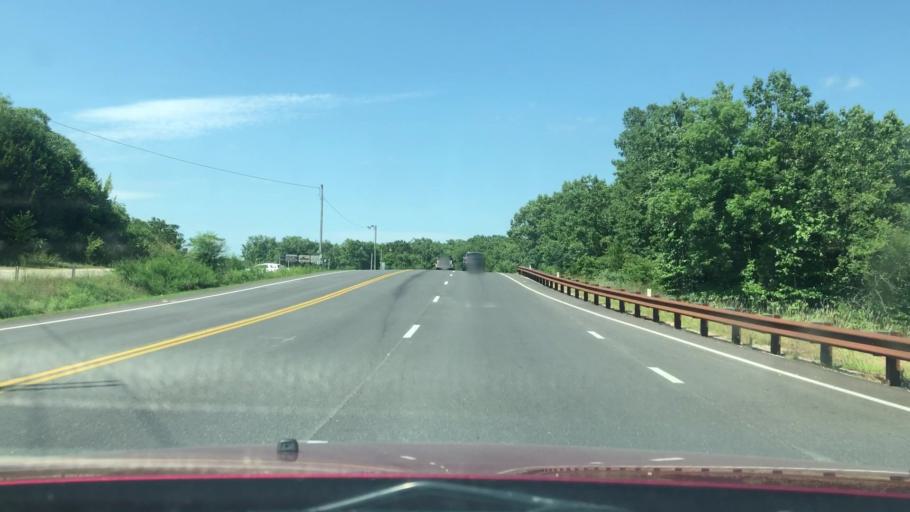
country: US
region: Missouri
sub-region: Stone County
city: Kimberling City
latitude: 36.6625
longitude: -93.3371
